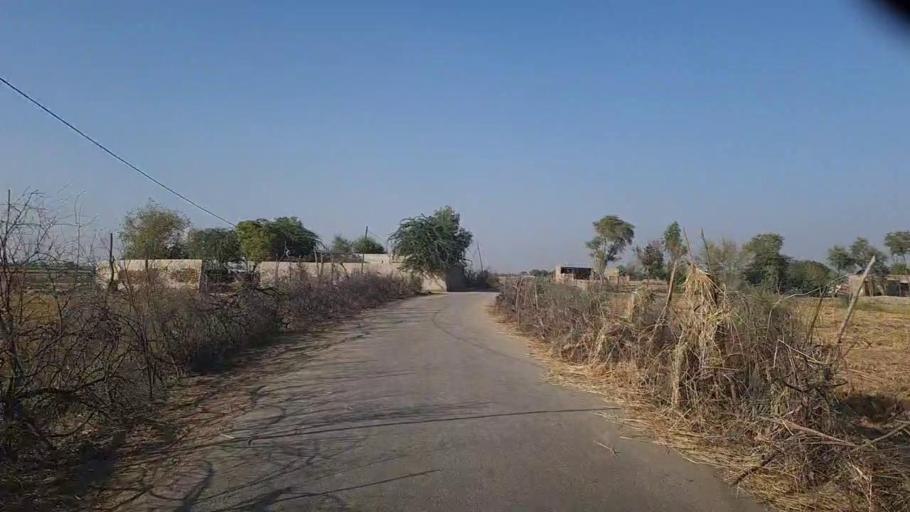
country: PK
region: Sindh
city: Tangwani
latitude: 28.2934
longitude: 68.9506
